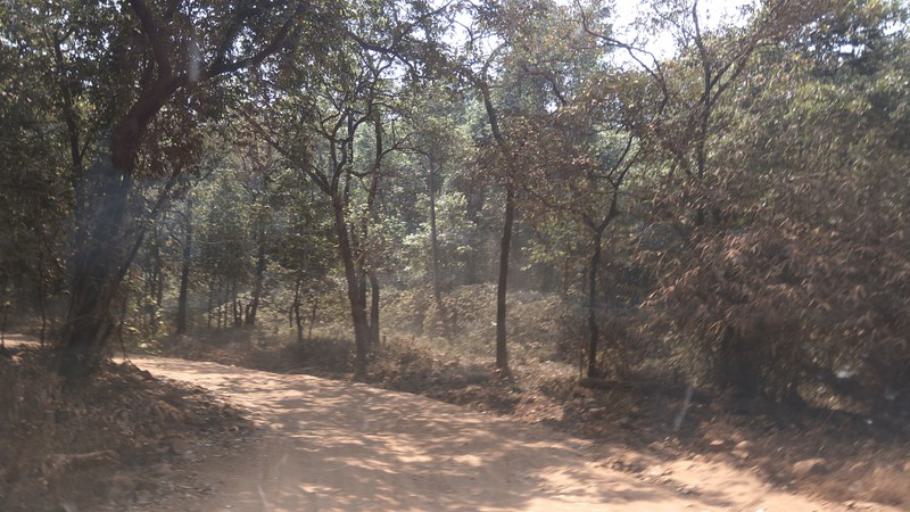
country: IN
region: Goa
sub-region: South Goa
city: Sanguem
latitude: 15.3250
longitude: 74.2841
